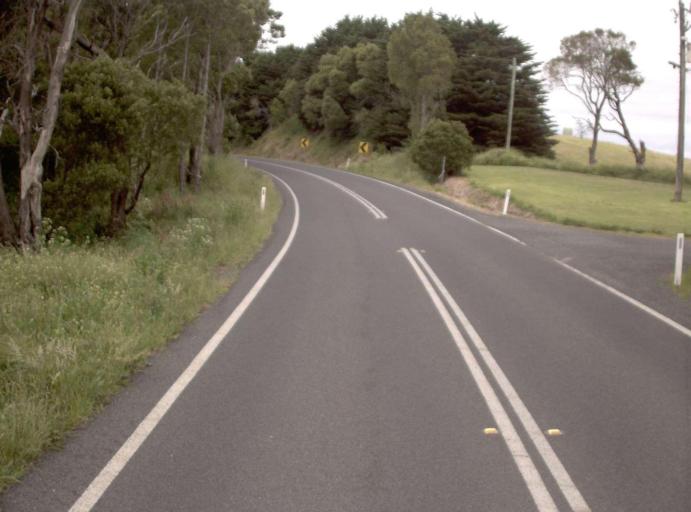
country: AU
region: Victoria
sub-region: Bass Coast
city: North Wonthaggi
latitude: -38.4840
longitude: 145.7521
